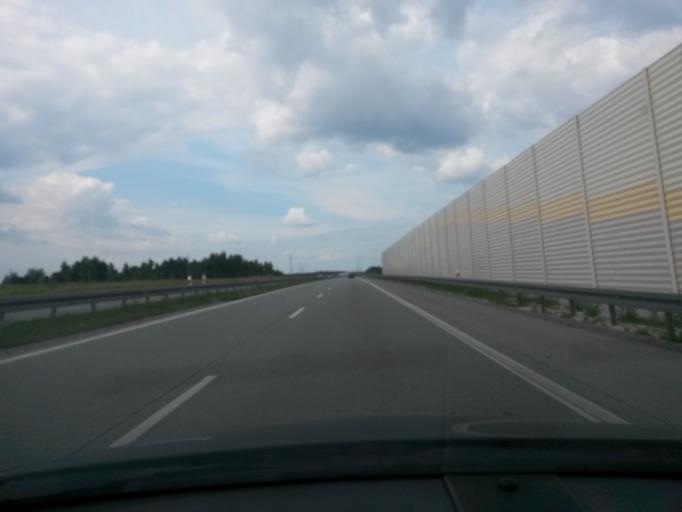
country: PL
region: Lodz Voivodeship
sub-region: Powiat skierniewicki
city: Kowiesy
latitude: 51.8565
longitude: 20.3755
